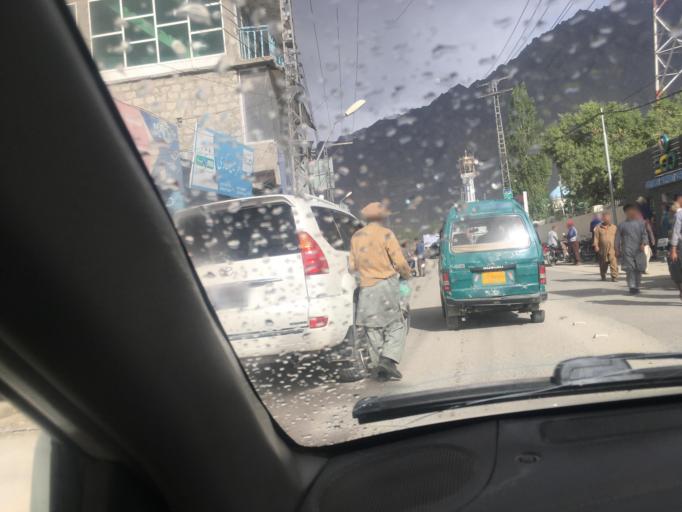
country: PK
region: Gilgit-Baltistan
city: Skardu
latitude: 35.2982
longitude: 75.6363
